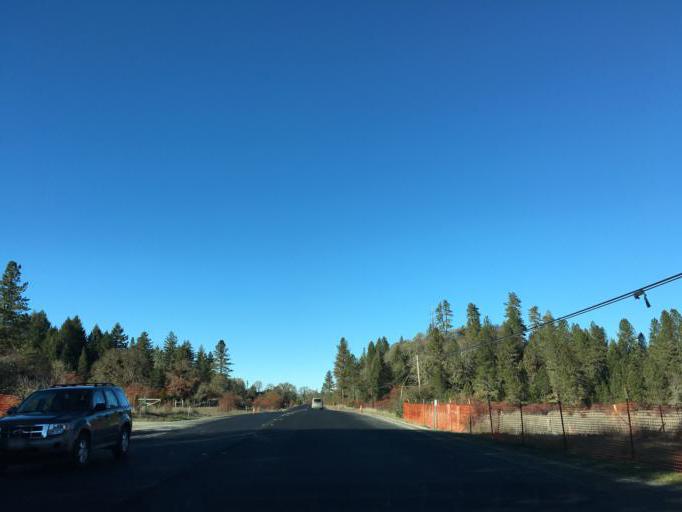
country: US
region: California
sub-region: Mendocino County
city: Laytonville
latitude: 39.6349
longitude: -123.4685
